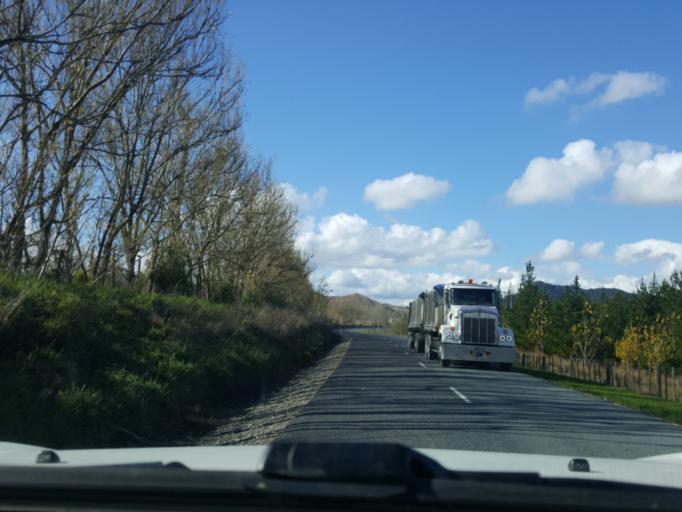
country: NZ
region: Waikato
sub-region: Waikato District
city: Te Kauwhata
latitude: -37.5313
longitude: 175.1824
